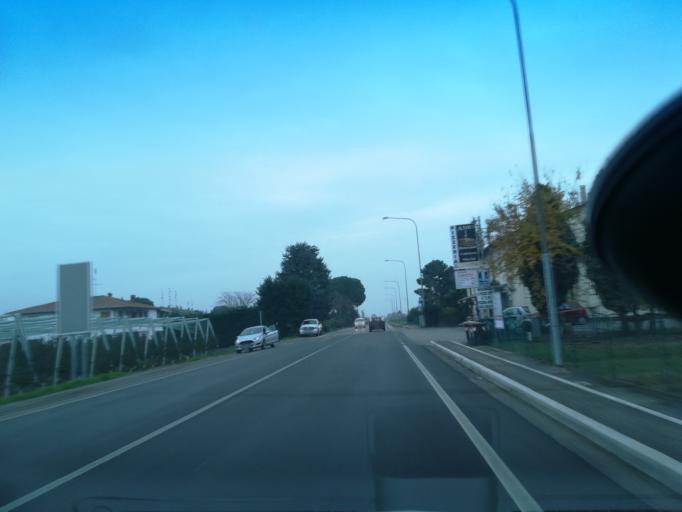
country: IT
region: Emilia-Romagna
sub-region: Provincia di Ravenna
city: Castel Bolognese
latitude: 44.3363
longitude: 11.7577
